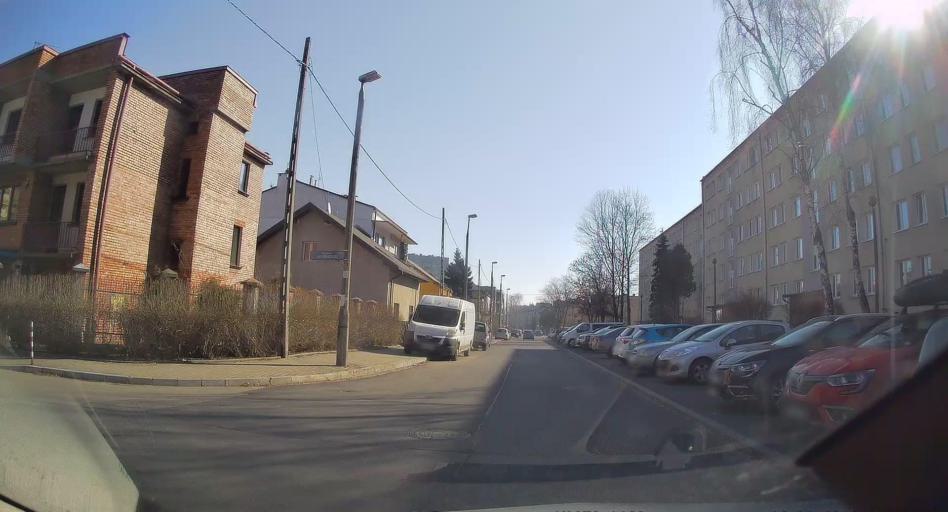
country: PL
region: Lesser Poland Voivodeship
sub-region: Krakow
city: Krakow
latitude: 50.0225
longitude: 19.9923
